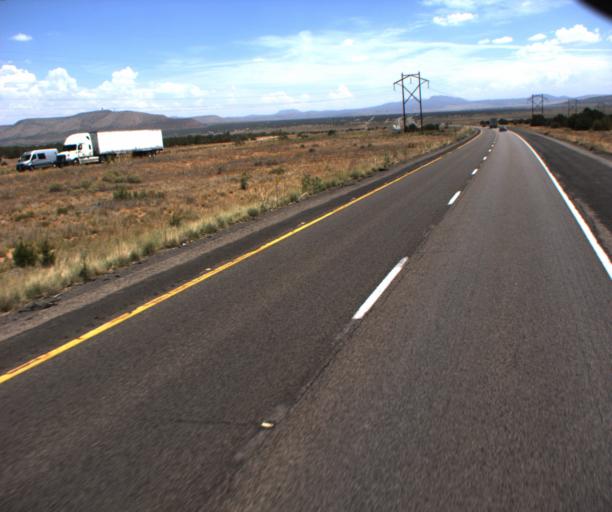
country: US
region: Arizona
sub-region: Mohave County
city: Peach Springs
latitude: 35.3029
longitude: -113.0010
